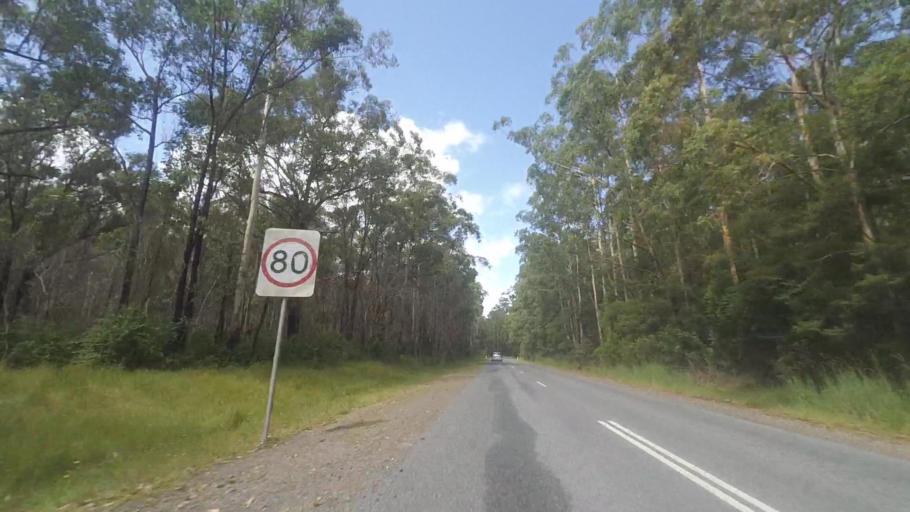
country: AU
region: New South Wales
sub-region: Great Lakes
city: Bulahdelah
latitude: -32.4019
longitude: 152.2831
